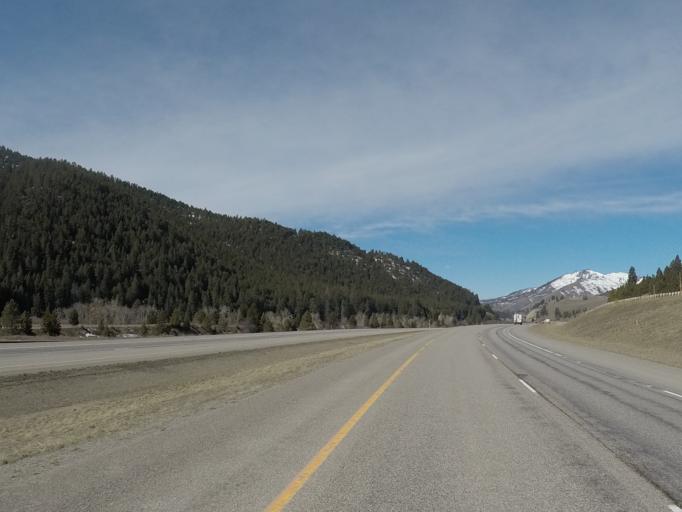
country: US
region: Montana
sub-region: Missoula County
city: Clinton
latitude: 46.7128
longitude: -113.5198
